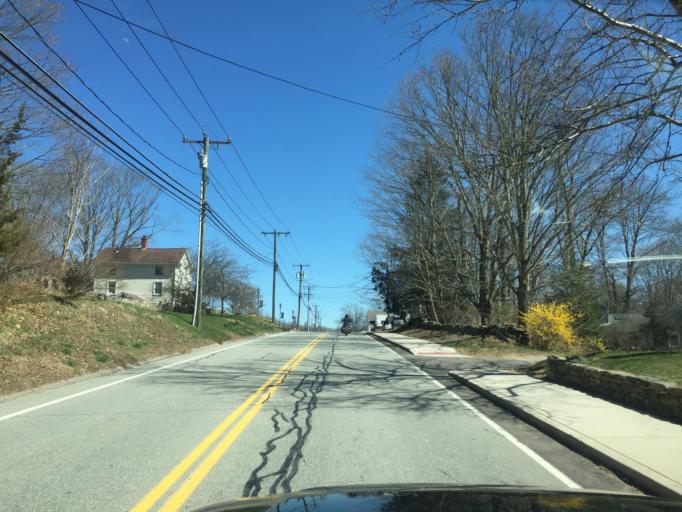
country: US
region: Connecticut
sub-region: Hartford County
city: Terramuggus
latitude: 41.6326
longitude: -72.4633
